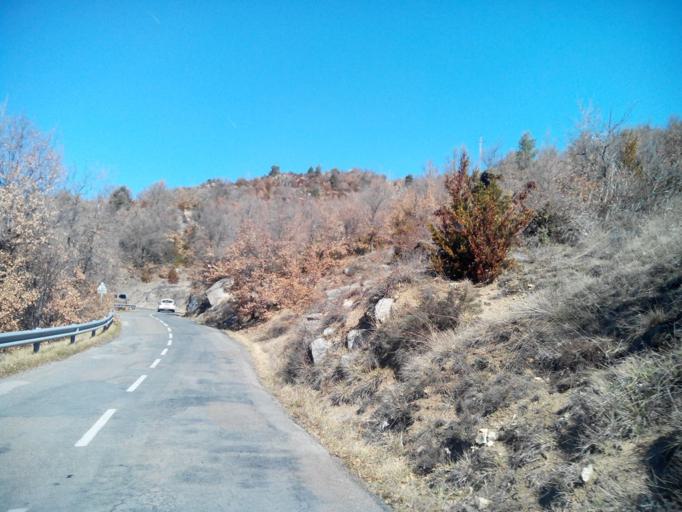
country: ES
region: Catalonia
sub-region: Provincia de Lleida
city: Lles de Cerdanya
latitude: 42.3790
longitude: 1.6909
